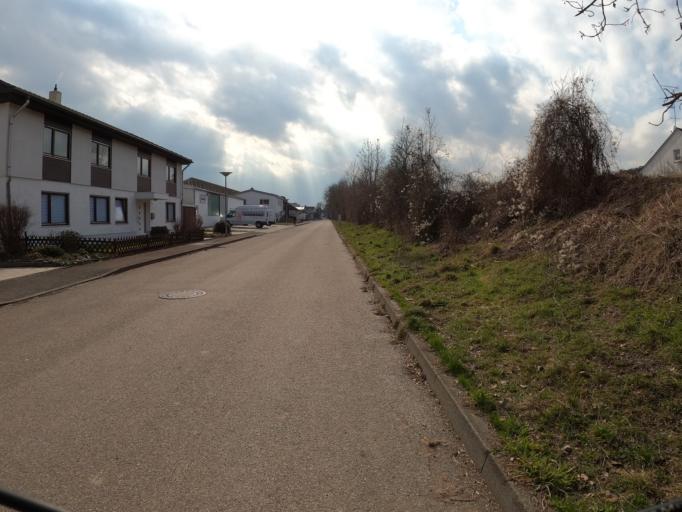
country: DE
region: Bavaria
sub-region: Swabia
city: Nersingen
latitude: 48.4395
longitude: 10.0608
